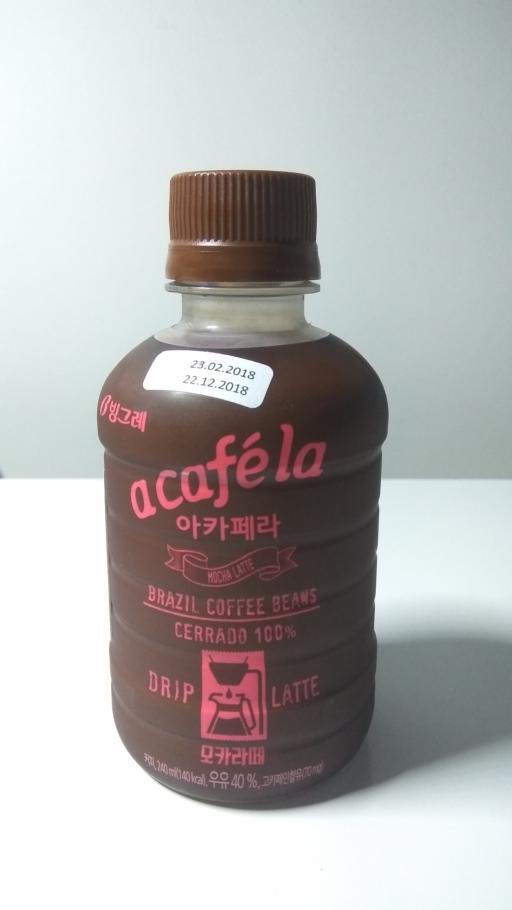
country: RU
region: Primorskiy
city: Russkiy
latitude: 43.0275
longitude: 131.8887
